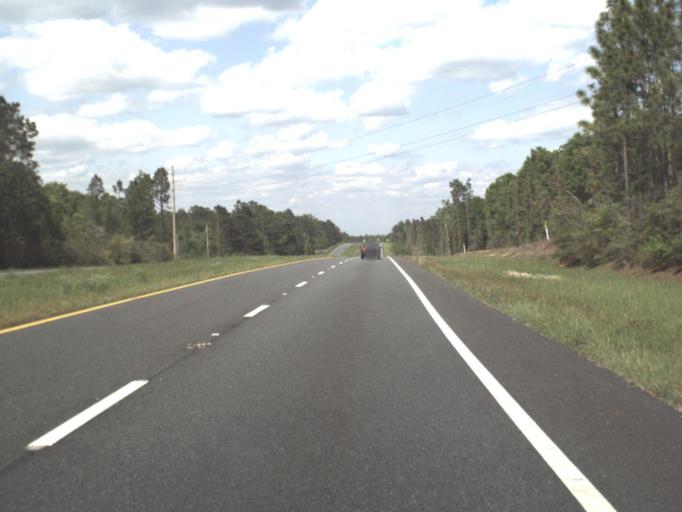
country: US
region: Florida
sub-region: Escambia County
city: Molino
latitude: 30.8302
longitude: -87.3316
